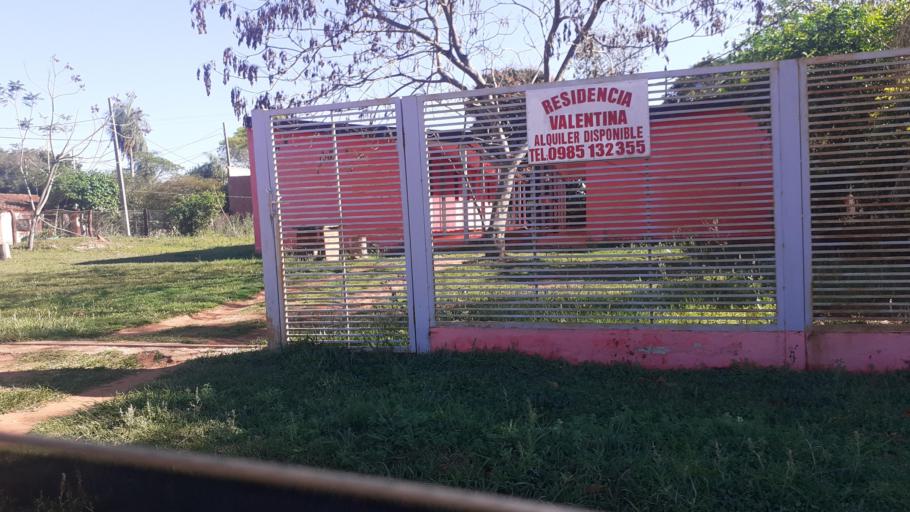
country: PY
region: Misiones
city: San Juan Bautista
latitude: -26.6658
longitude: -57.1281
